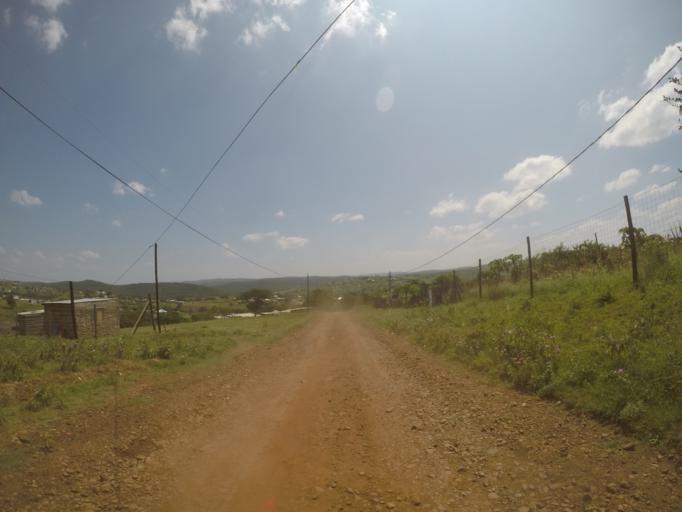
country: ZA
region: KwaZulu-Natal
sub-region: uThungulu District Municipality
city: Empangeni
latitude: -28.5945
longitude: 31.7387
